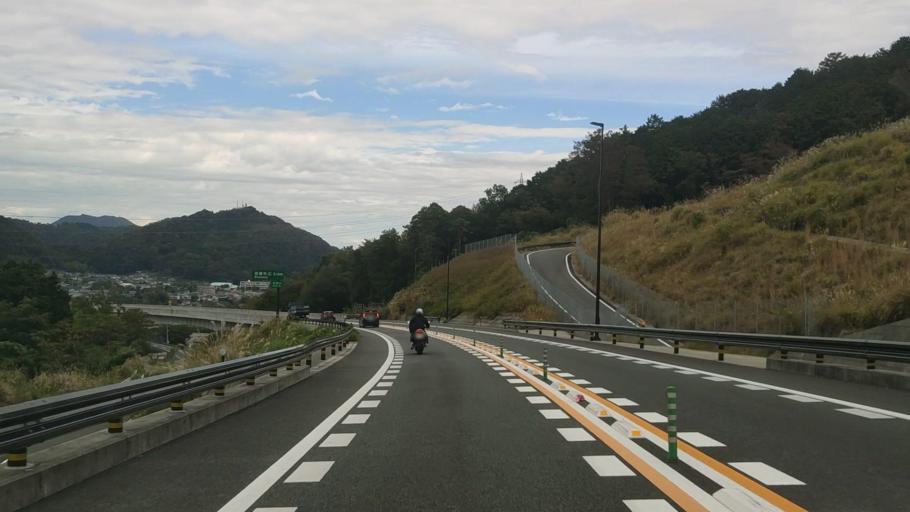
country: JP
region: Shizuoka
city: Ito
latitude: 34.9560
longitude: 138.9469
